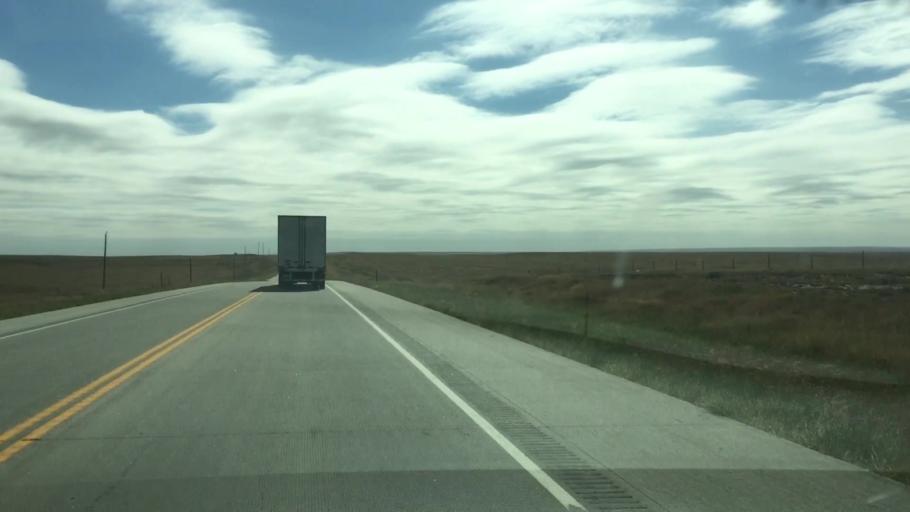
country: US
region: Colorado
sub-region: Lincoln County
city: Hugo
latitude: 39.0072
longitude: -103.2945
